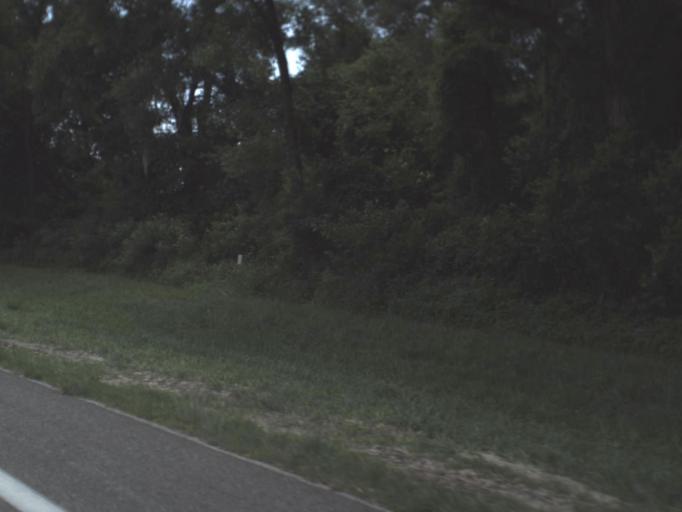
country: US
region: Florida
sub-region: Lafayette County
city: Mayo
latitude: 30.0353
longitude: -83.0659
